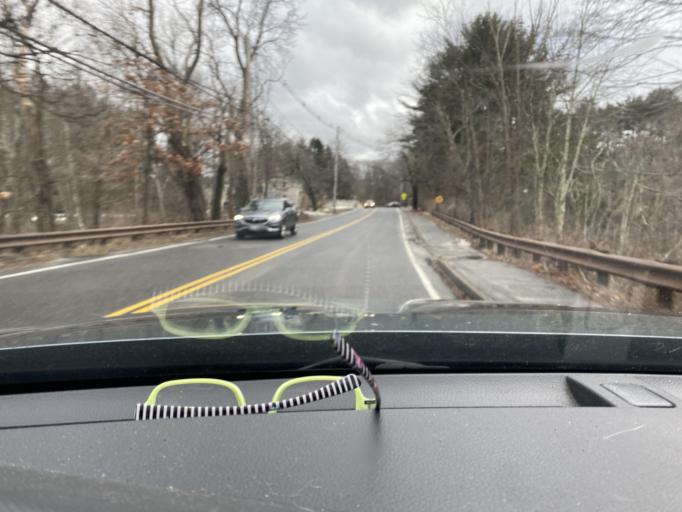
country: US
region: Massachusetts
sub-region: Middlesex County
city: Sherborn
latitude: 42.2287
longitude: -71.3662
